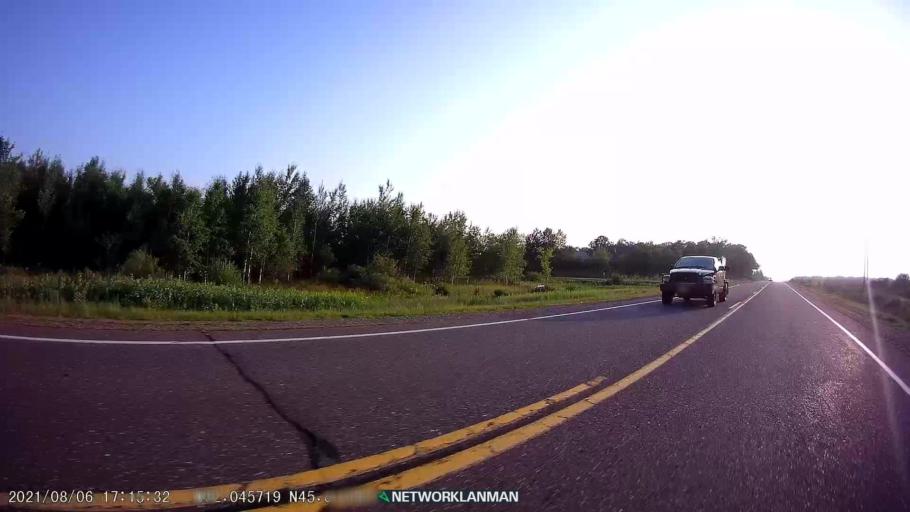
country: US
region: Wisconsin
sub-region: Washburn County
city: Shell Lake
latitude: 45.8154
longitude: -92.0461
